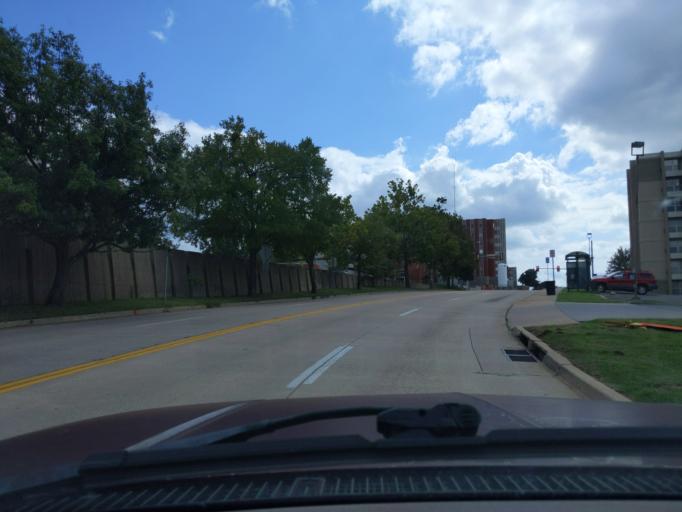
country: US
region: Oklahoma
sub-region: Tulsa County
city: Tulsa
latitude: 36.1490
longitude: -96.0010
